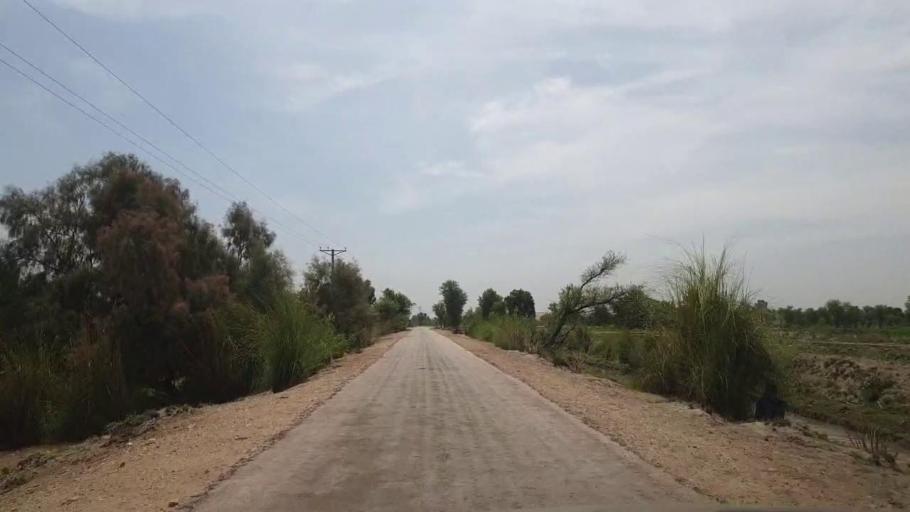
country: PK
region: Sindh
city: Kot Diji
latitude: 27.1114
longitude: 69.0198
